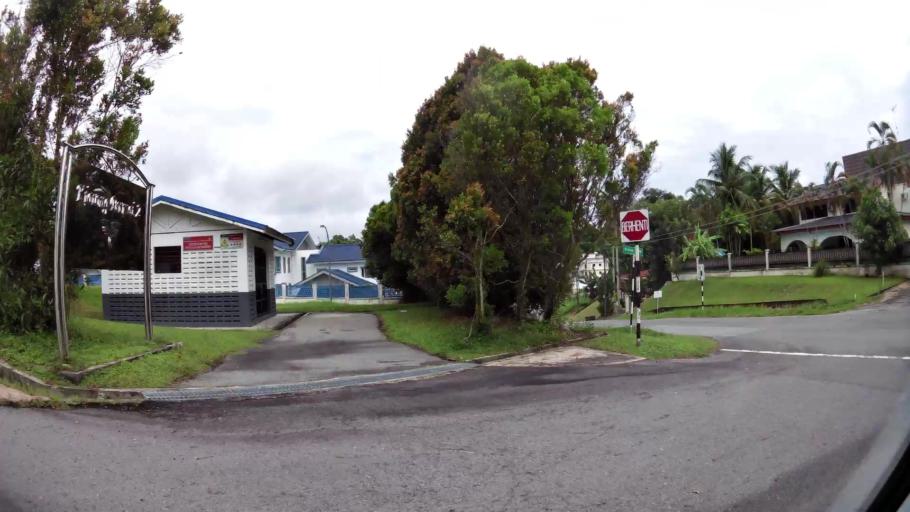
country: BN
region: Brunei and Muara
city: Bandar Seri Begawan
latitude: 4.8888
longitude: 114.9230
